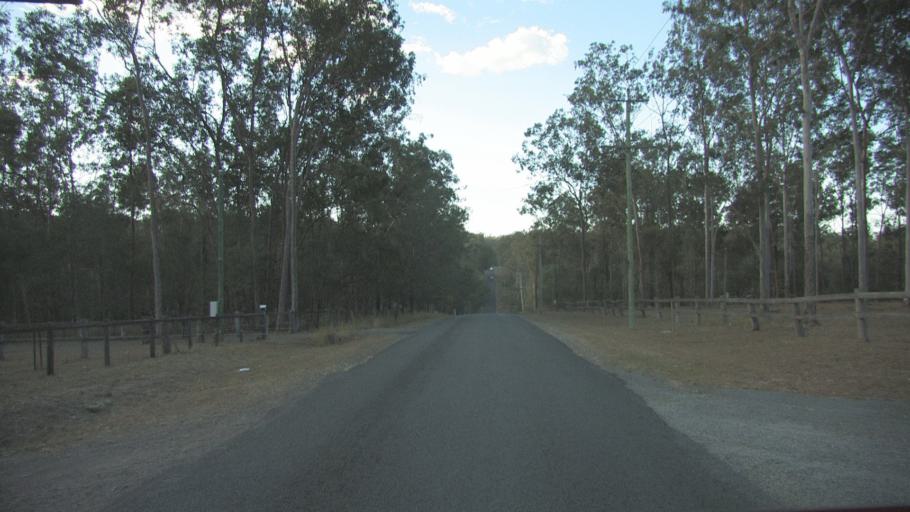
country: AU
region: Queensland
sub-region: Logan
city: Cedar Vale
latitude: -27.8512
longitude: 153.0896
